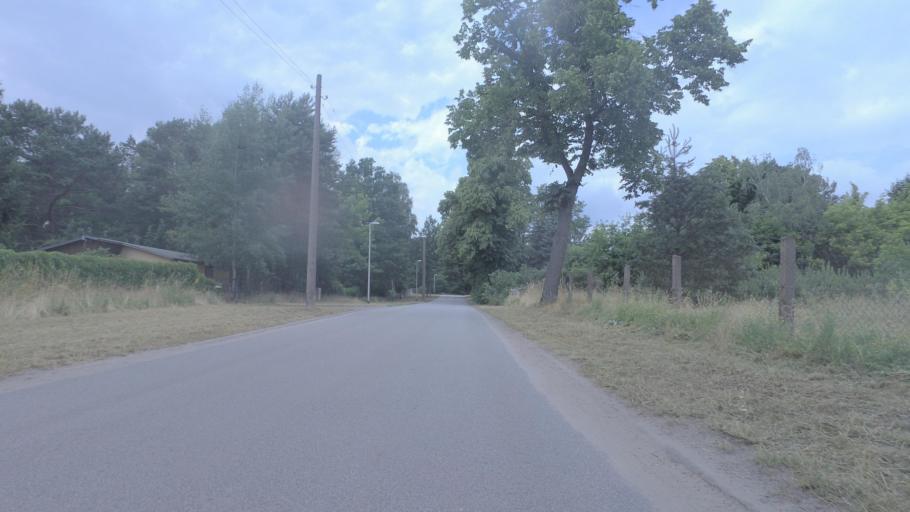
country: DE
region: Brandenburg
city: Zossen
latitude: 52.1384
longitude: 13.4735
